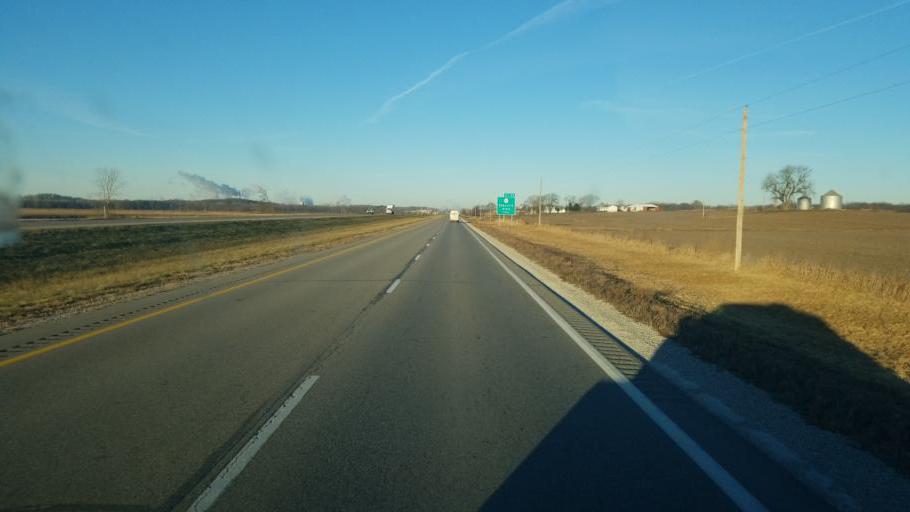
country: US
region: Iowa
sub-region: Wapello County
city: Eddyville
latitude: 41.1389
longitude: -92.5957
